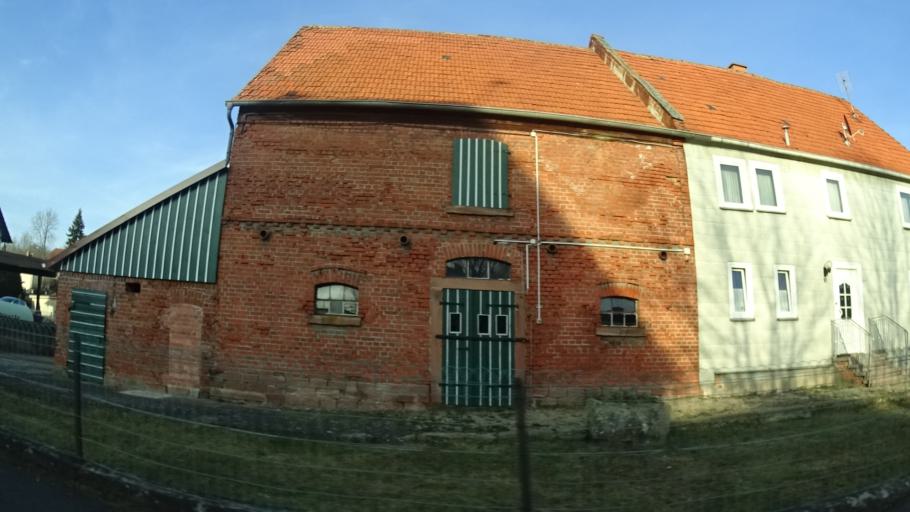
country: DE
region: Bavaria
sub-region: Regierungsbezirk Unterfranken
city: Zeitlofs
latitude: 50.3128
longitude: 9.6217
